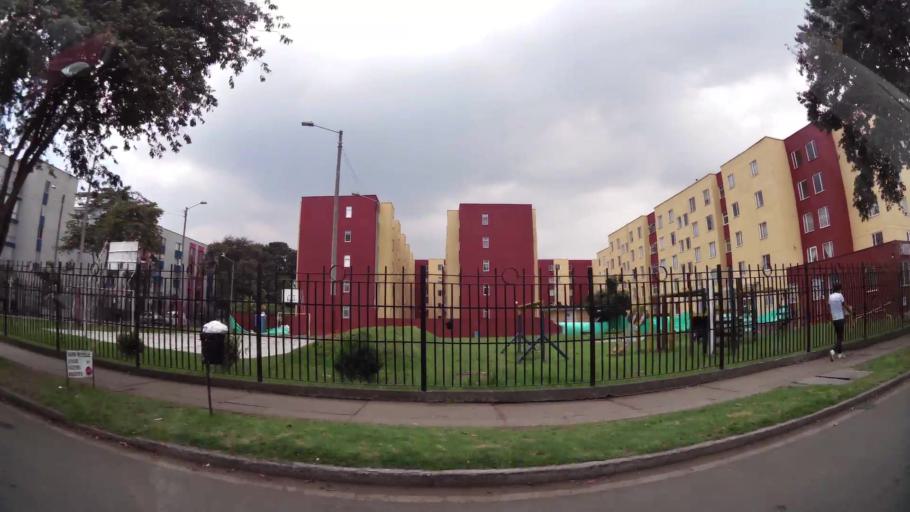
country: CO
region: Cundinamarca
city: Cota
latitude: 4.7483
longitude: -74.0492
